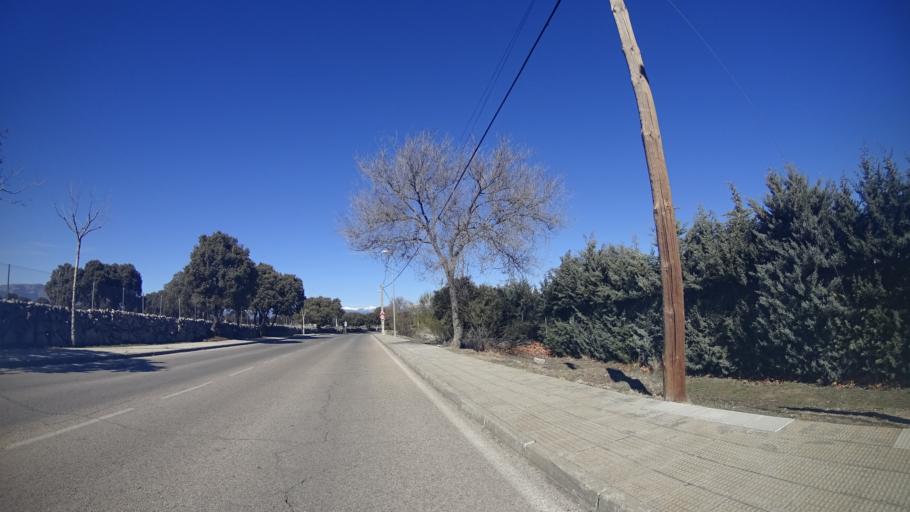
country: ES
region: Madrid
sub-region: Provincia de Madrid
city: Colmenarejo
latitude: 40.5503
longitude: -4.0134
